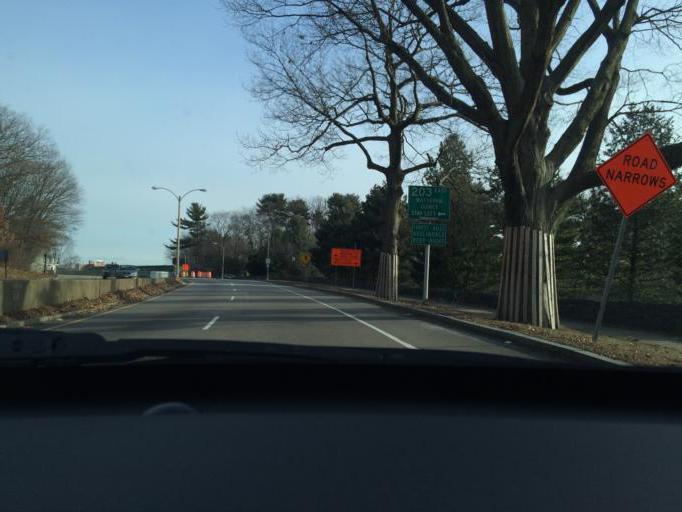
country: US
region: Massachusetts
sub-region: Suffolk County
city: Jamaica Plain
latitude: 42.3029
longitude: -71.1185
